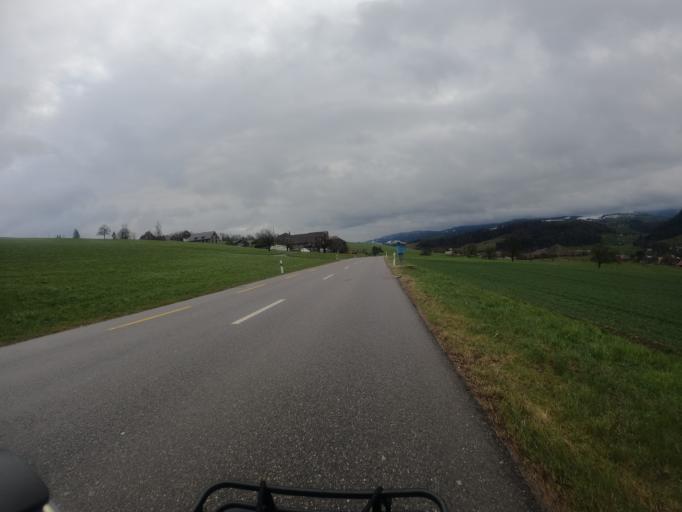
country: CH
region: Zurich
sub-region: Bezirk Affoltern
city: Hausen am Albis / Hausen (Dorf)
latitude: 47.2229
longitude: 8.5548
